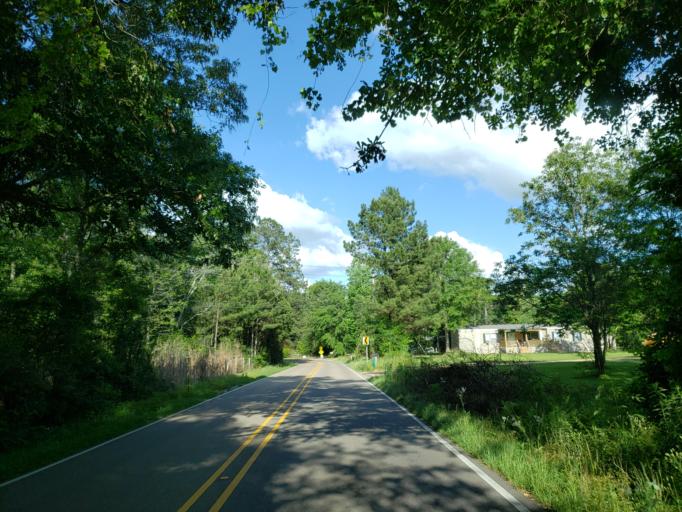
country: US
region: Mississippi
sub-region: Lamar County
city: West Hattiesburg
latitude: 31.2706
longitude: -89.4104
